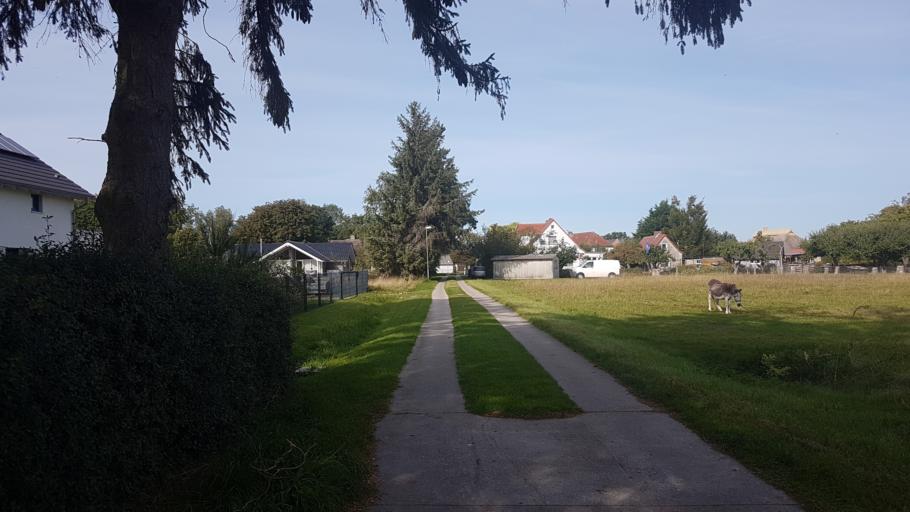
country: DE
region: Mecklenburg-Vorpommern
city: Gingst
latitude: 54.4467
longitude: 13.1835
